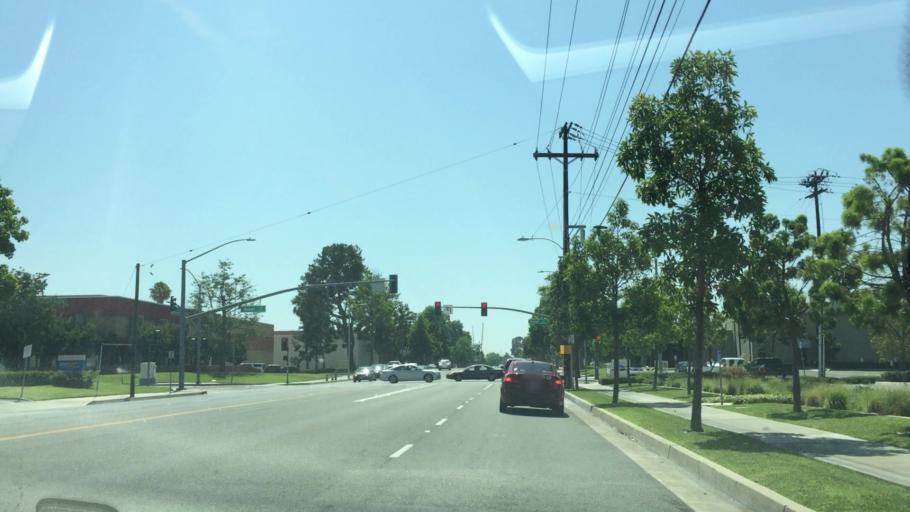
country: US
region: California
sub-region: Orange County
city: Fountain Valley
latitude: 33.7088
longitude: -117.9119
